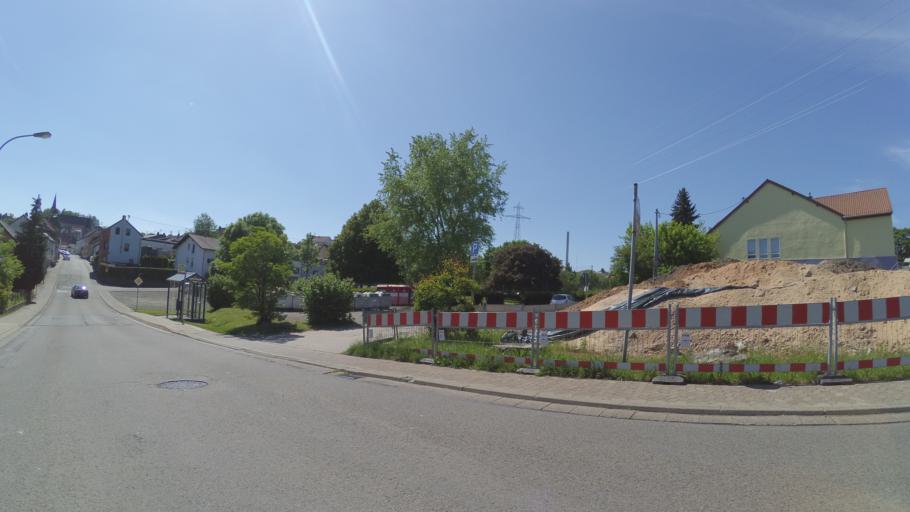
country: DE
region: Saarland
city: Quierschied
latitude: 49.3293
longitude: 7.0569
